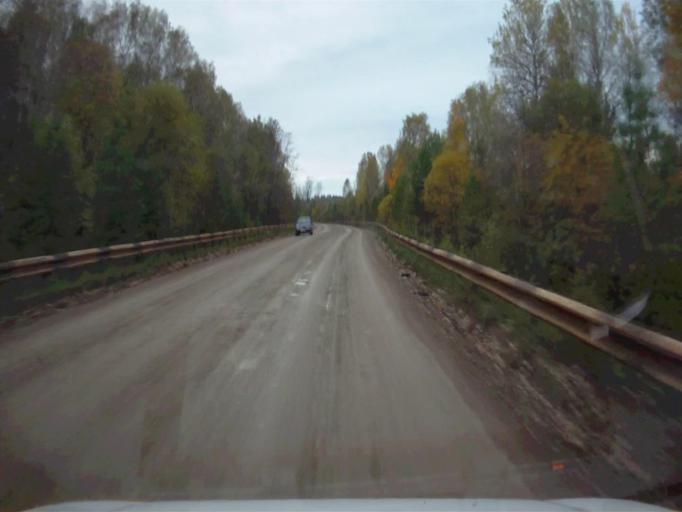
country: RU
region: Chelyabinsk
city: Nyazepetrovsk
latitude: 56.1289
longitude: 59.3290
